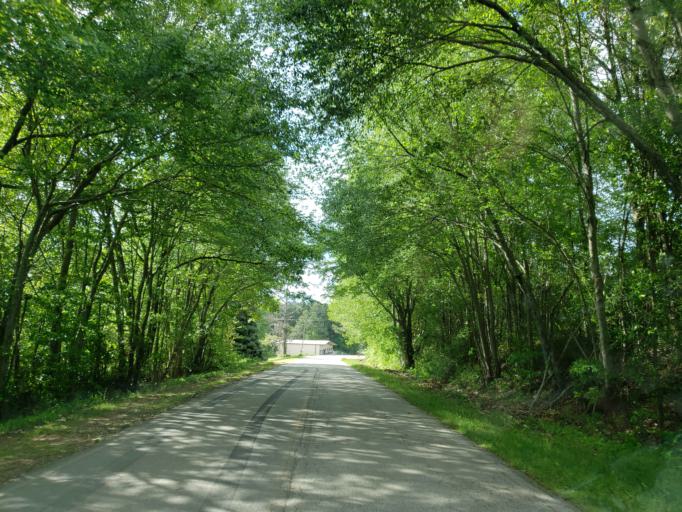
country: US
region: Georgia
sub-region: Haralson County
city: Tallapoosa
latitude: 33.6762
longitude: -85.2909
